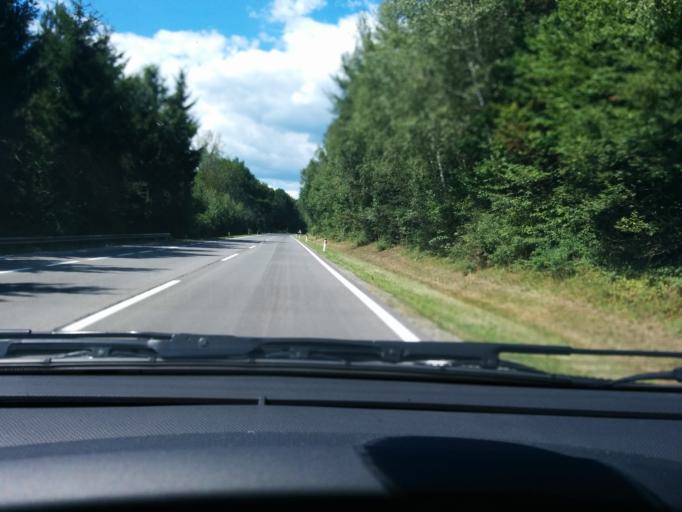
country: AT
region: Styria
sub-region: Politischer Bezirk Hartberg-Fuerstenfeld
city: Hartberg
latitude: 47.3087
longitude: 15.9828
